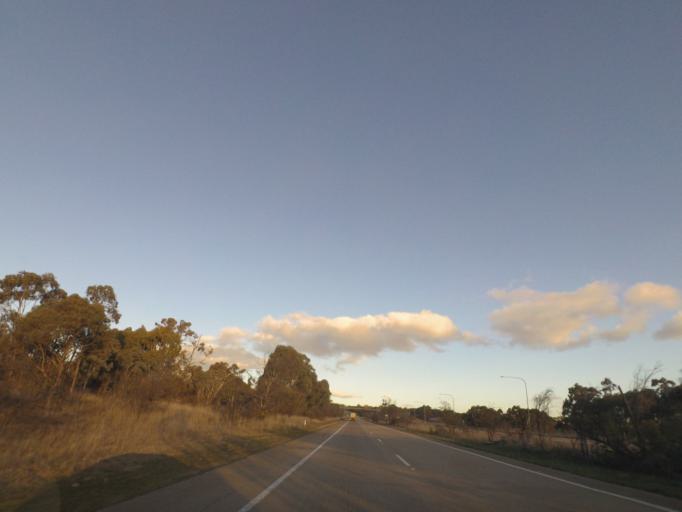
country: AU
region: New South Wales
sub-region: Yass Valley
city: Yass
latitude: -34.7977
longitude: 148.8728
